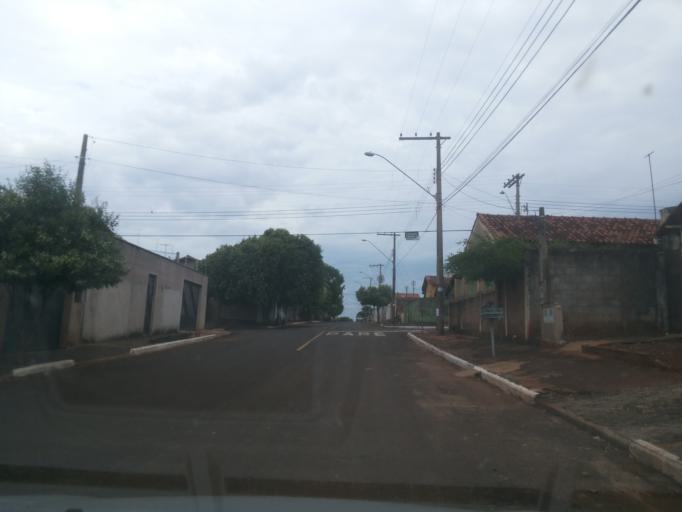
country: BR
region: Minas Gerais
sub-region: Ituiutaba
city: Ituiutaba
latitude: -18.9695
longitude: -49.4737
